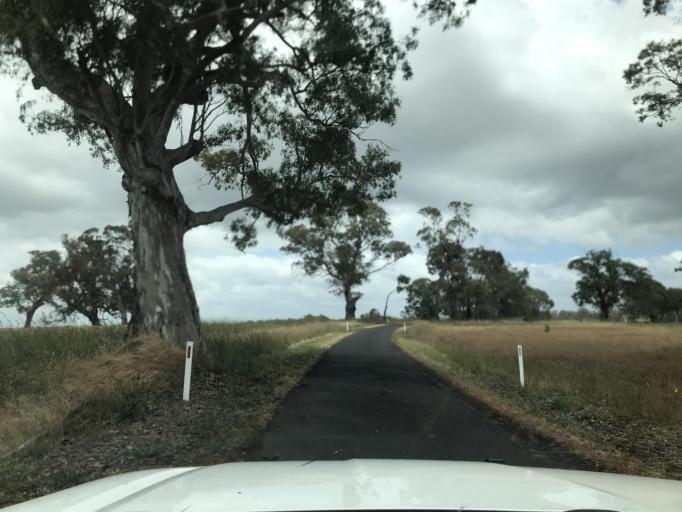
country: AU
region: South Australia
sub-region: Wattle Range
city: Penola
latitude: -37.2607
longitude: 141.5211
